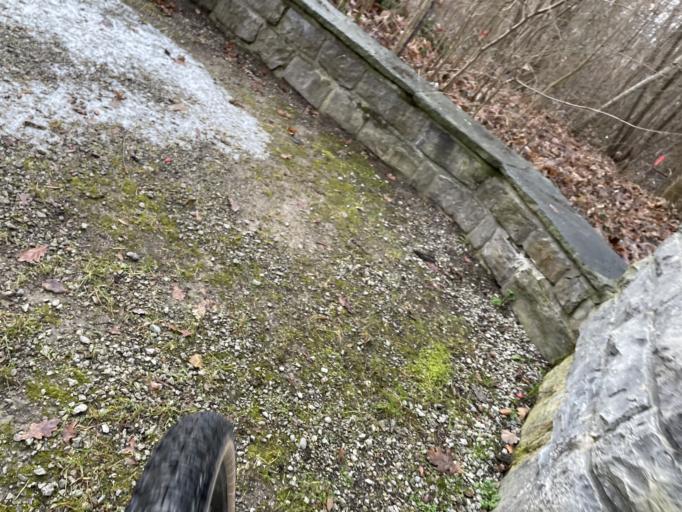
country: CH
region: Bern
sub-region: Bern-Mittelland District
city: Munsingen
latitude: 46.8664
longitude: 7.5471
